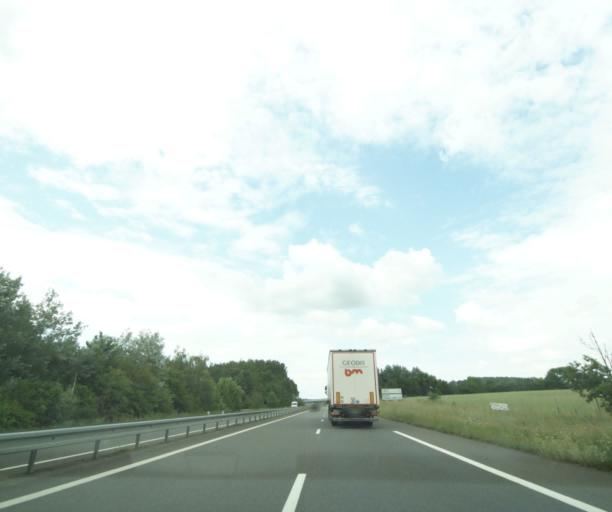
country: FR
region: Pays de la Loire
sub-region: Departement de Maine-et-Loire
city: Vivy
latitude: 47.3216
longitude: -0.0358
